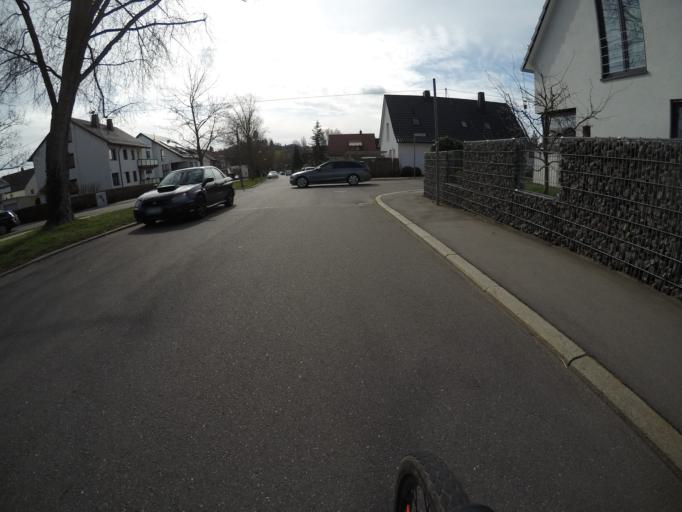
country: DE
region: Baden-Wuerttemberg
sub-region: Regierungsbezirk Stuttgart
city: Sindelfingen
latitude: 48.7066
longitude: 9.0120
